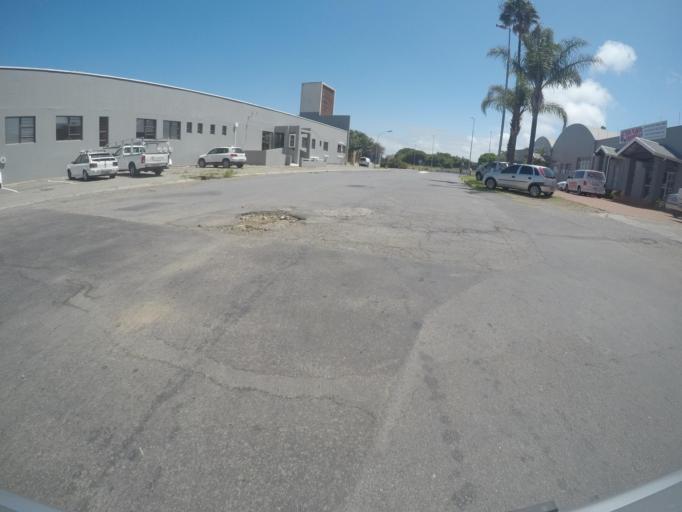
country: ZA
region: Eastern Cape
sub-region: Buffalo City Metropolitan Municipality
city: East London
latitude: -33.0103
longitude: 27.9152
